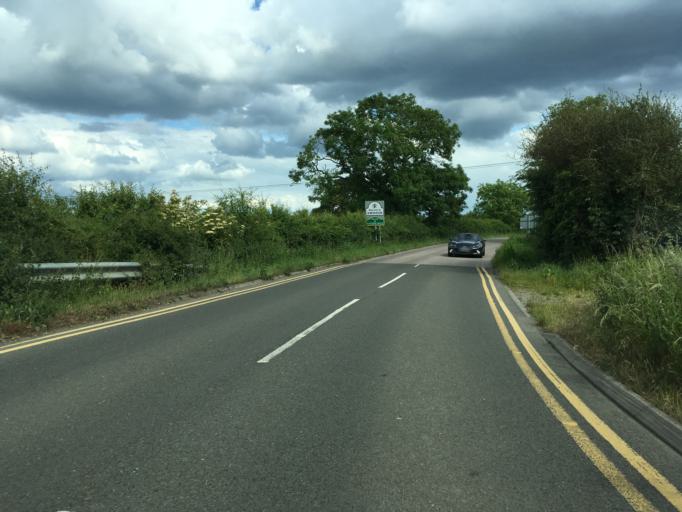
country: GB
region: England
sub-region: Wiltshire
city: Purton
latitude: 51.6062
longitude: -1.8410
